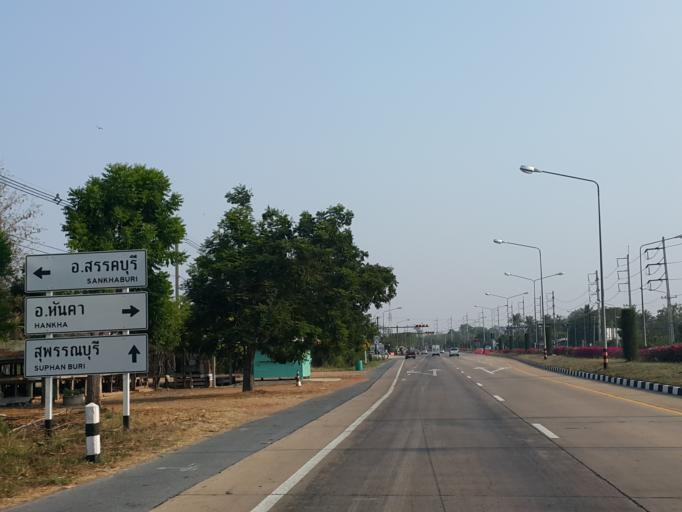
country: TH
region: Chai Nat
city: Hankha
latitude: 14.9461
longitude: 100.0819
